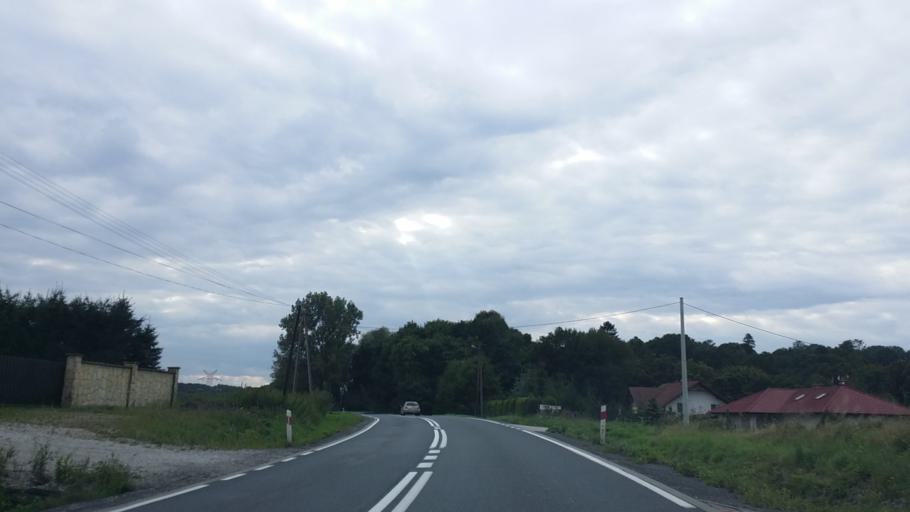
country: PL
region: Lesser Poland Voivodeship
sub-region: Powiat wadowicki
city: Brzeznica
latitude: 49.9642
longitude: 19.6100
